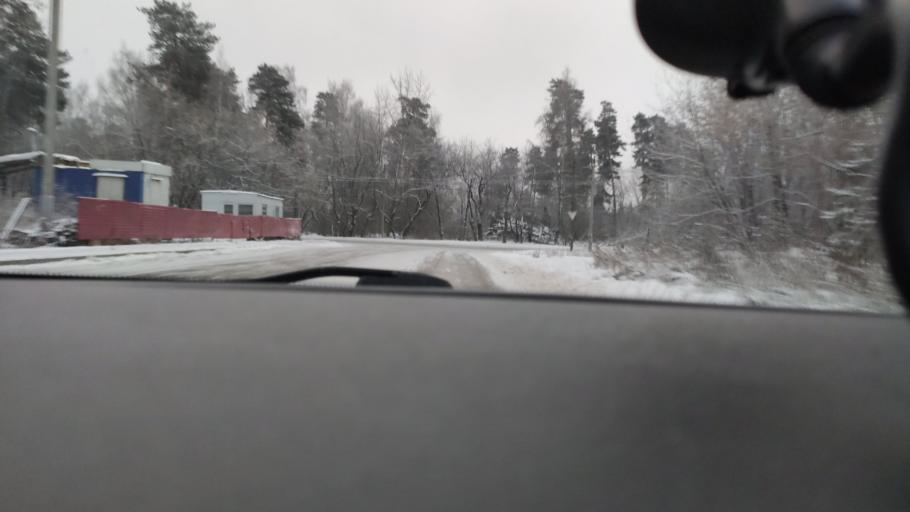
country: RU
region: Perm
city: Kondratovo
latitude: 58.0201
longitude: 56.0066
